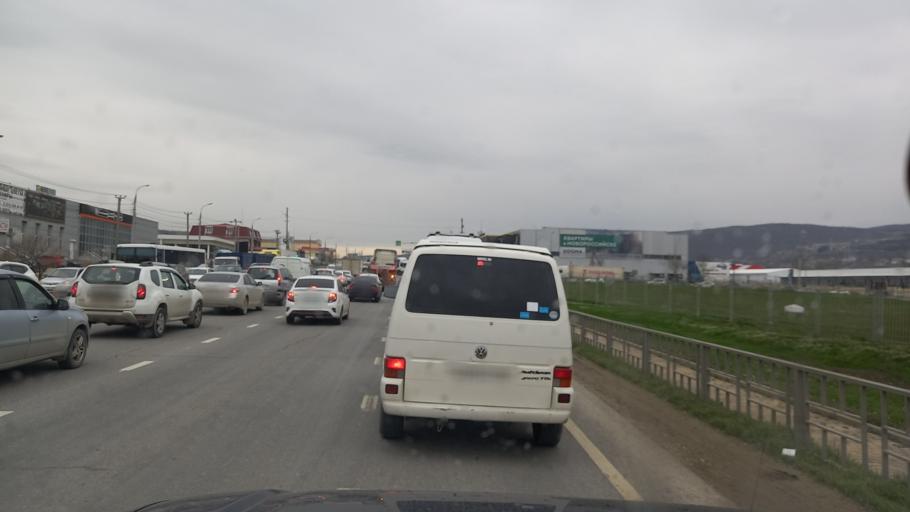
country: RU
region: Krasnodarskiy
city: Gayduk
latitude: 44.7710
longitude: 37.6971
